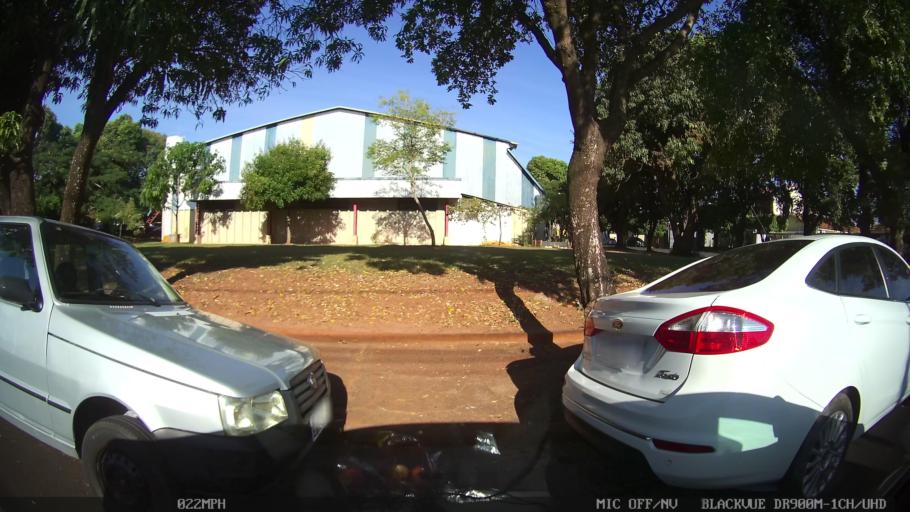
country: BR
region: Sao Paulo
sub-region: Sao Jose Do Rio Preto
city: Sao Jose do Rio Preto
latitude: -20.7953
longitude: -49.3652
